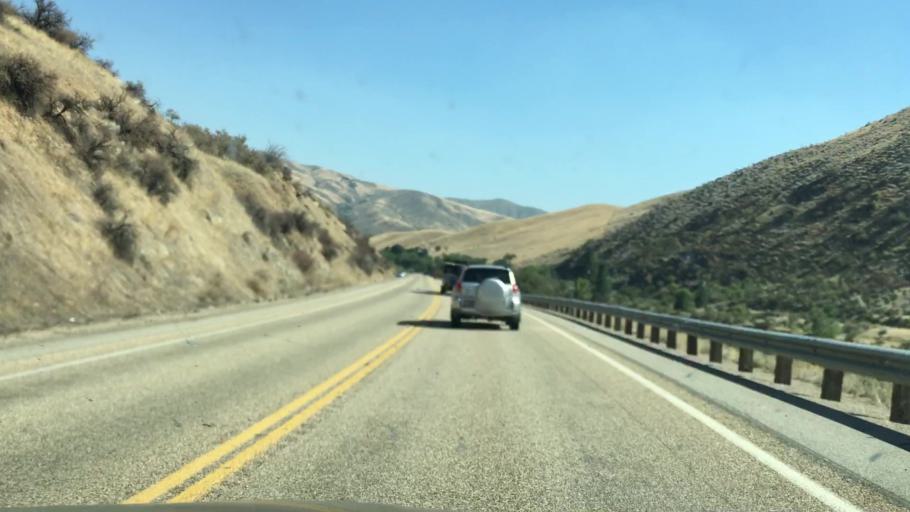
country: US
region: Idaho
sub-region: Ada County
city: Eagle
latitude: 43.9423
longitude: -116.1960
